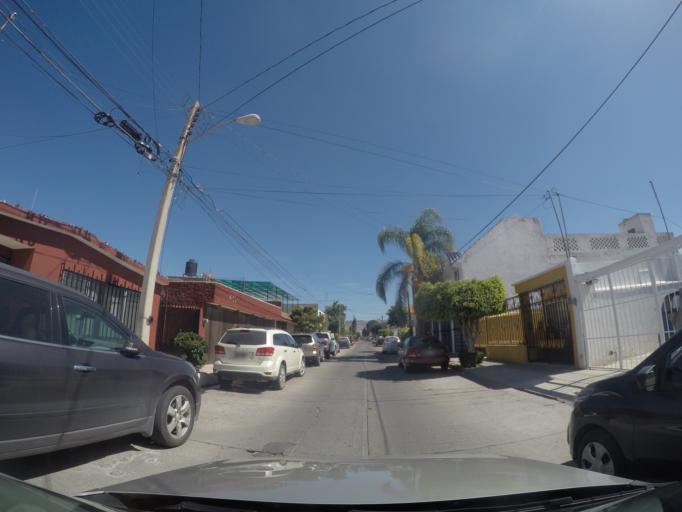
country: MX
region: San Luis Potosi
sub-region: San Luis Potosi
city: San Luis Potosi
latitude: 22.1537
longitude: -101.0089
